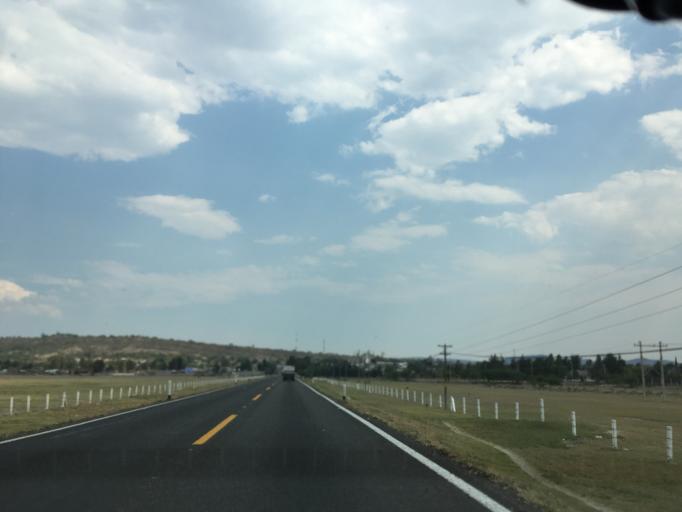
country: MX
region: Michoacan
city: Cuitzeo del Porvenir
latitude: 19.9787
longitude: -101.1429
